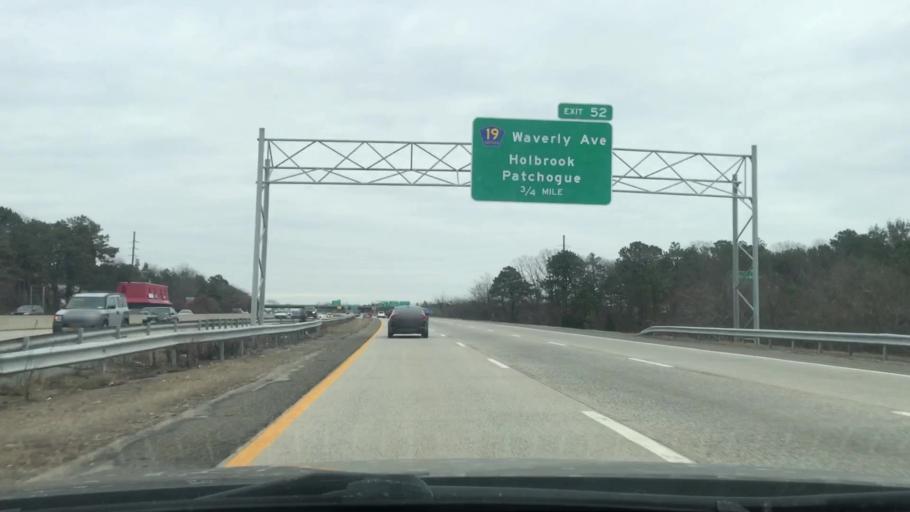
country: US
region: New York
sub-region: Suffolk County
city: Bayport
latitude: 40.7699
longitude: -73.0545
